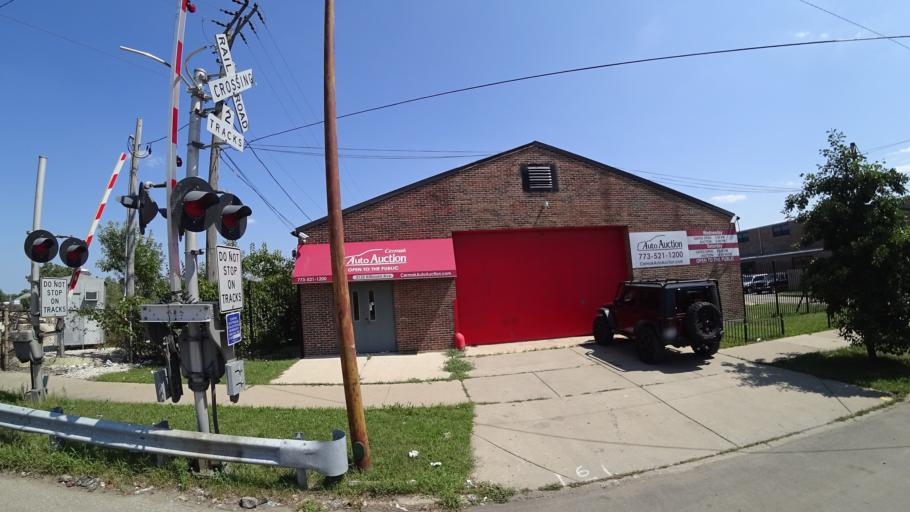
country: US
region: Illinois
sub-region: Cook County
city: Cicero
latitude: 41.8522
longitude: -87.7369
